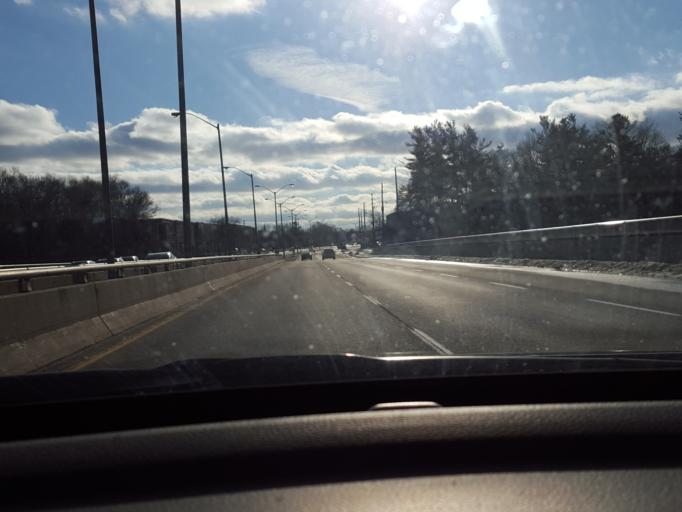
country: CA
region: Ontario
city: Scarborough
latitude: 43.7800
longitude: -79.1708
